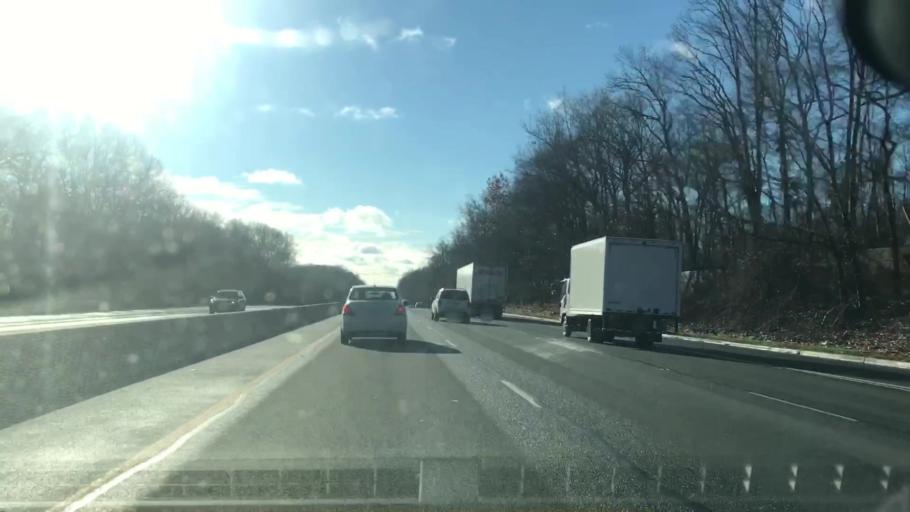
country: US
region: New Jersey
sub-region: Bergen County
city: Saddle River
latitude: 41.0301
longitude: -74.1108
